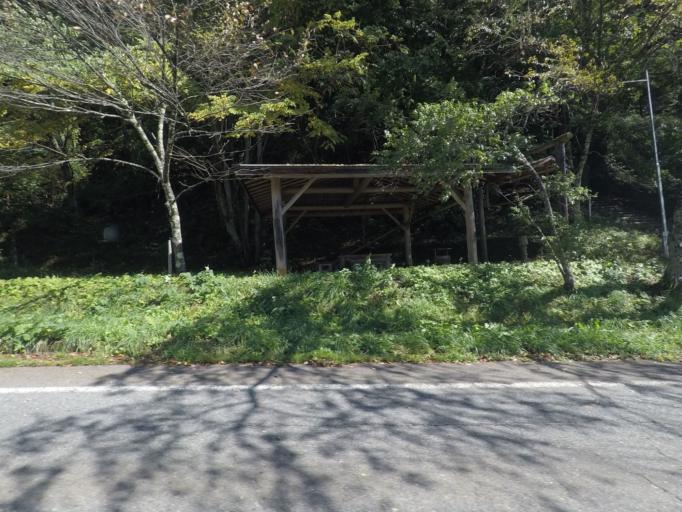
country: JP
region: Nagano
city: Shiojiri
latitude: 35.9928
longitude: 137.7403
